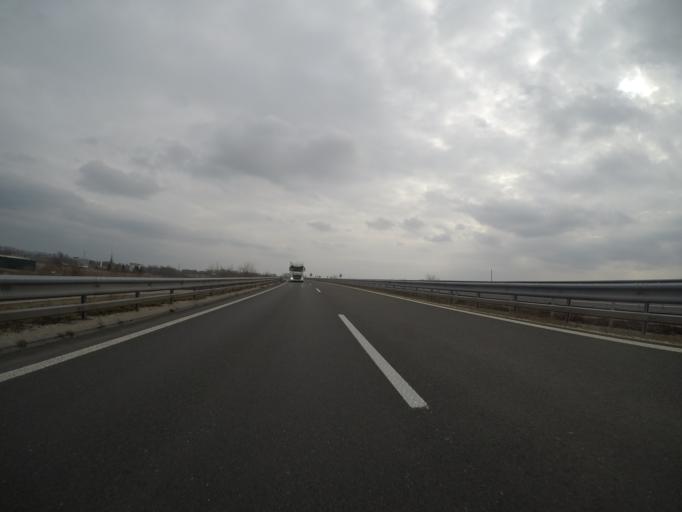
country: SI
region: Lendava-Lendva
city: Lendava
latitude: 46.5378
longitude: 16.4425
